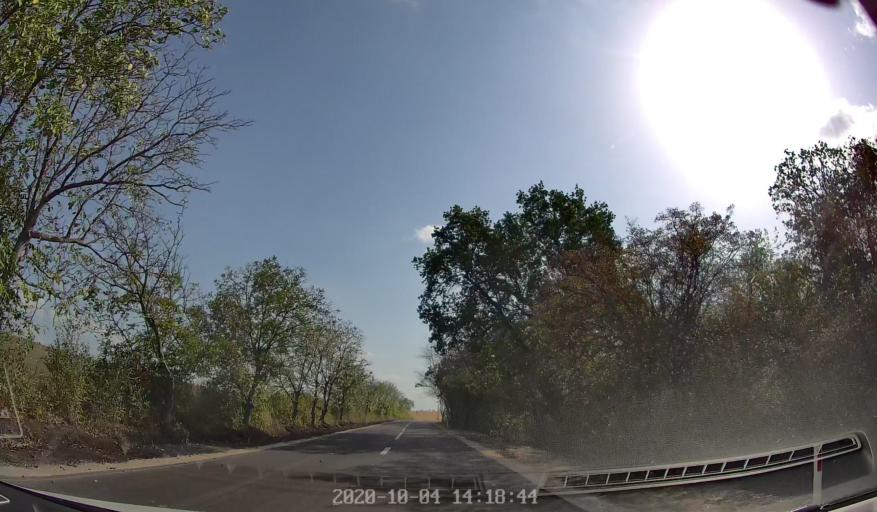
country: MD
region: Rezina
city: Saharna
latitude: 47.5970
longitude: 28.9765
